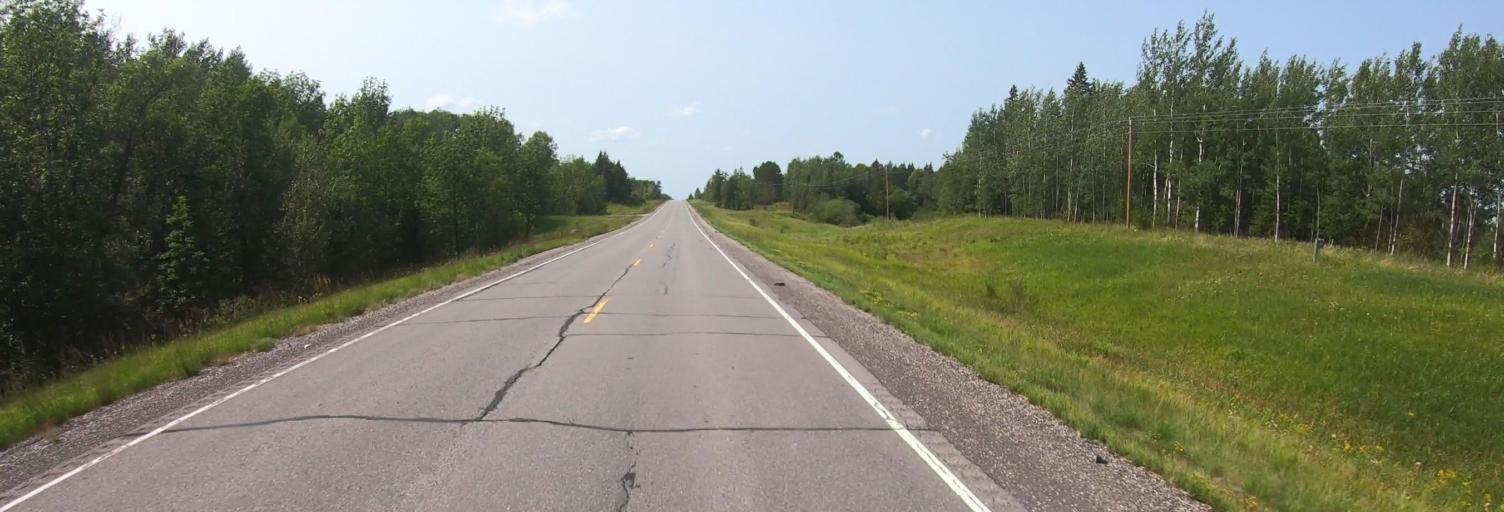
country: US
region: Minnesota
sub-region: Lake of the Woods County
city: Baudette
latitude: 48.6996
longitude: -94.3671
